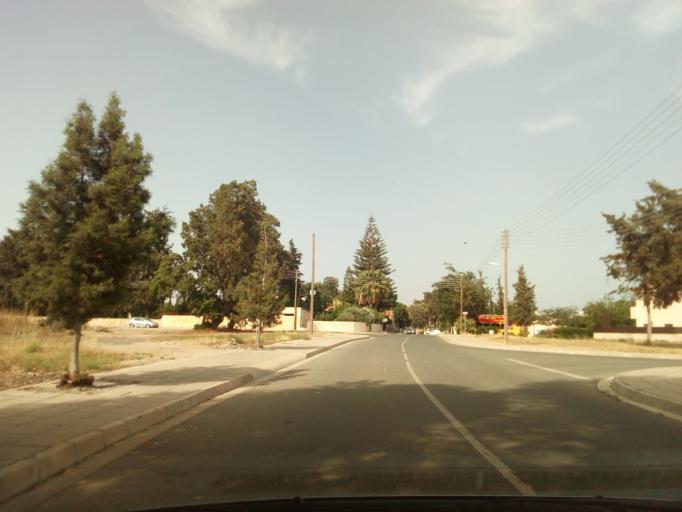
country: CY
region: Larnaka
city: Kiti
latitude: 34.8466
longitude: 33.5698
